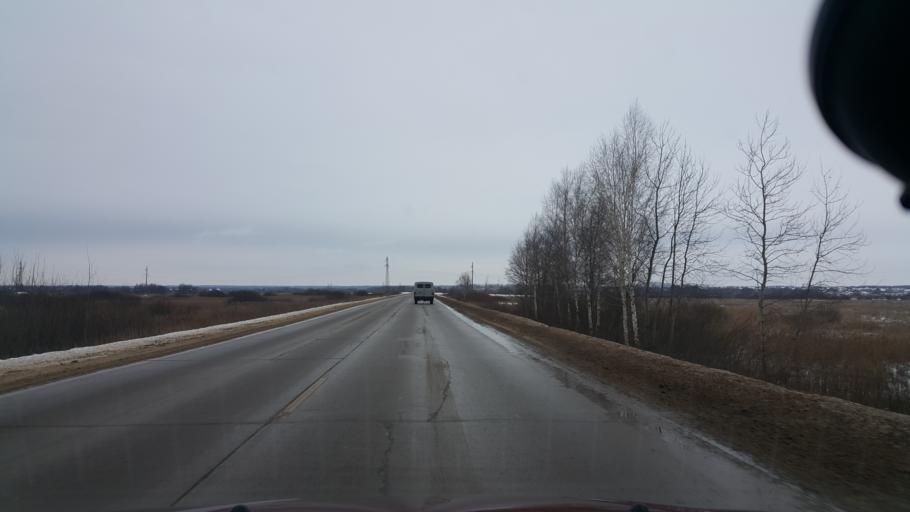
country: RU
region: Tambov
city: Bokino
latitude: 52.6245
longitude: 41.4869
